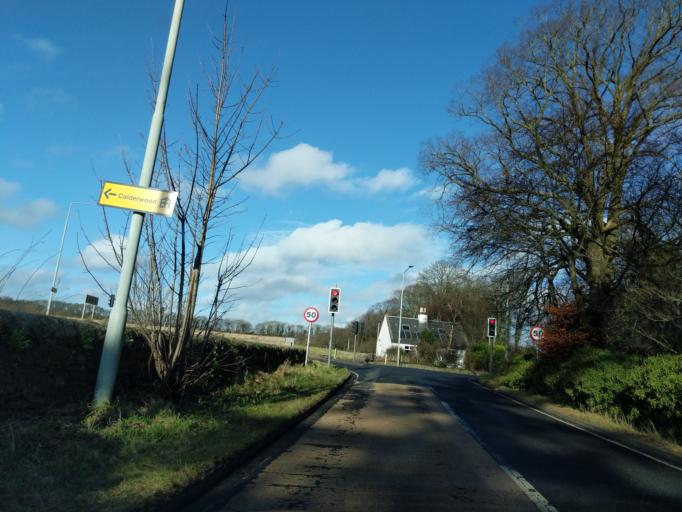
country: GB
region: Scotland
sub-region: West Lothian
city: Kirknewton
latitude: 55.9005
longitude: -3.3973
